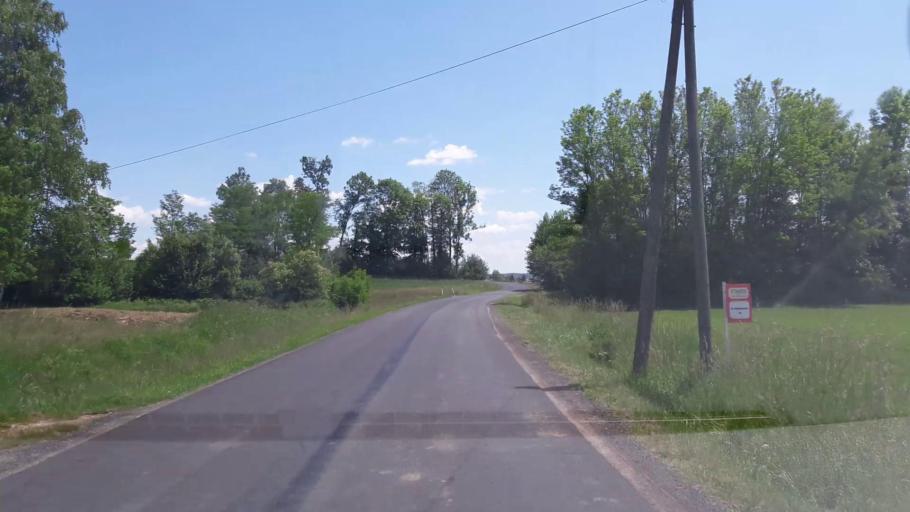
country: AT
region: Burgenland
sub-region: Politischer Bezirk Jennersdorf
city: Jennersdorf
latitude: 46.9590
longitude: 16.1114
